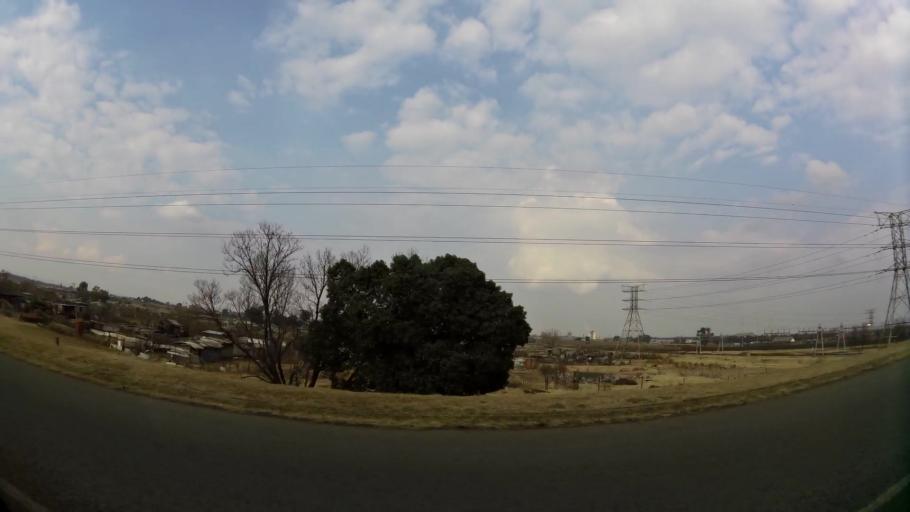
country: ZA
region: Gauteng
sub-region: Sedibeng District Municipality
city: Vereeniging
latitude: -26.6745
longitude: 27.8981
